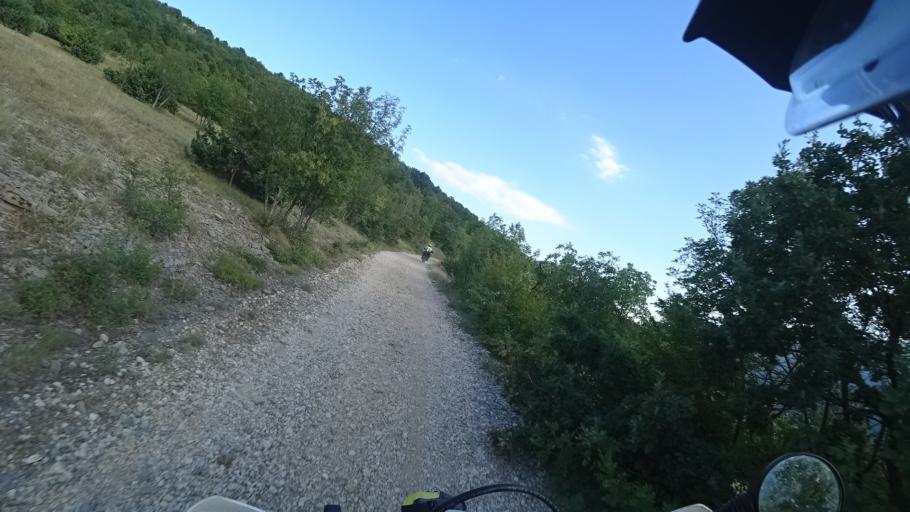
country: HR
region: Sibensko-Kniniska
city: Knin
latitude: 44.1789
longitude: 16.0688
